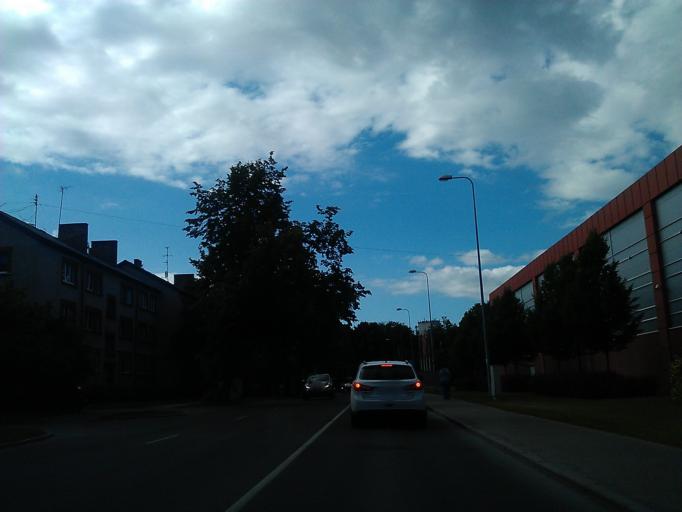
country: LV
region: Riga
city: Jaunciems
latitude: 56.9820
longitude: 24.2017
